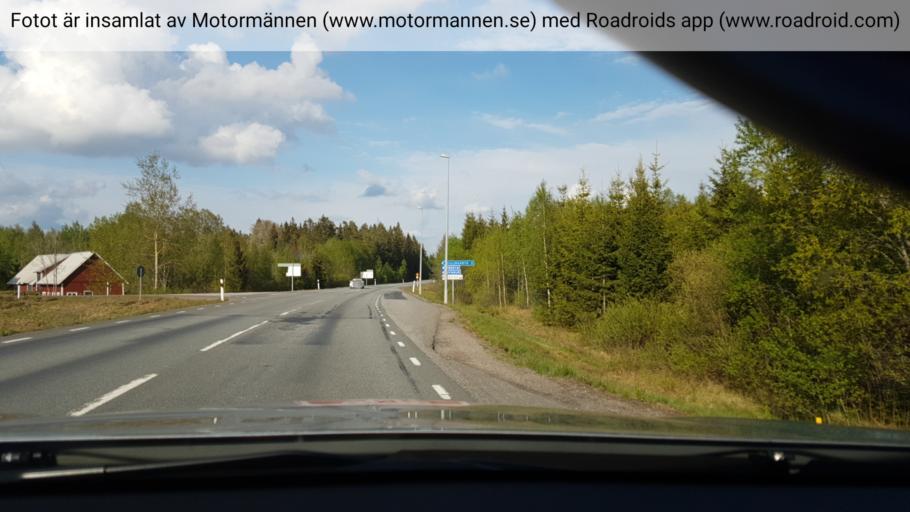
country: SE
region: Joenkoeping
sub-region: Vaggeryds Kommun
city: Skillingaryd
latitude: 57.4135
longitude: 14.0746
